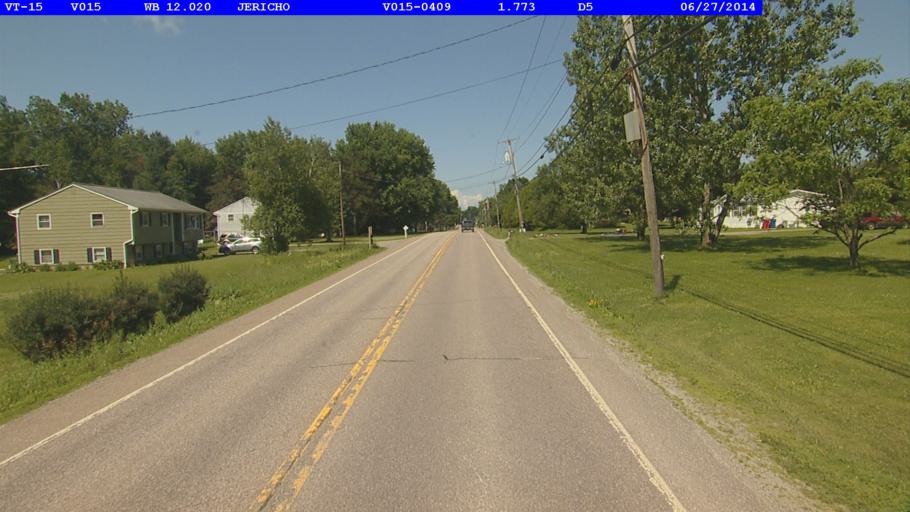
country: US
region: Vermont
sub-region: Chittenden County
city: Jericho
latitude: 44.5098
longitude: -72.9734
